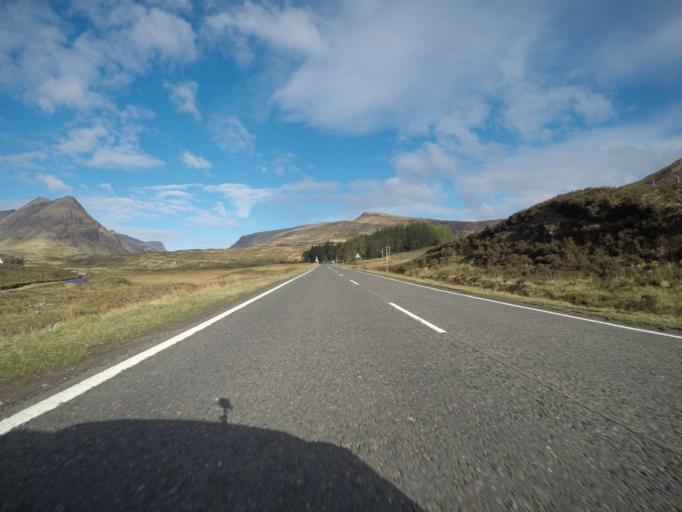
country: GB
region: Scotland
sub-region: Highland
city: Spean Bridge
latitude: 56.6635
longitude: -4.8987
